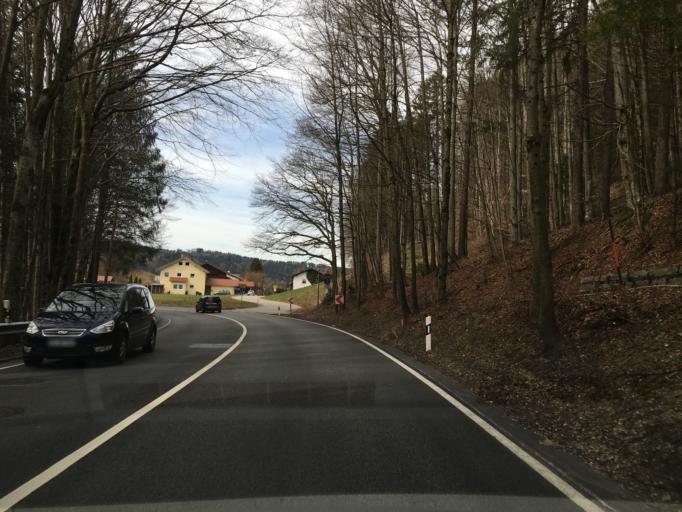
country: DE
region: Bavaria
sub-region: Upper Bavaria
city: Inzell
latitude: 47.7984
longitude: 12.7138
